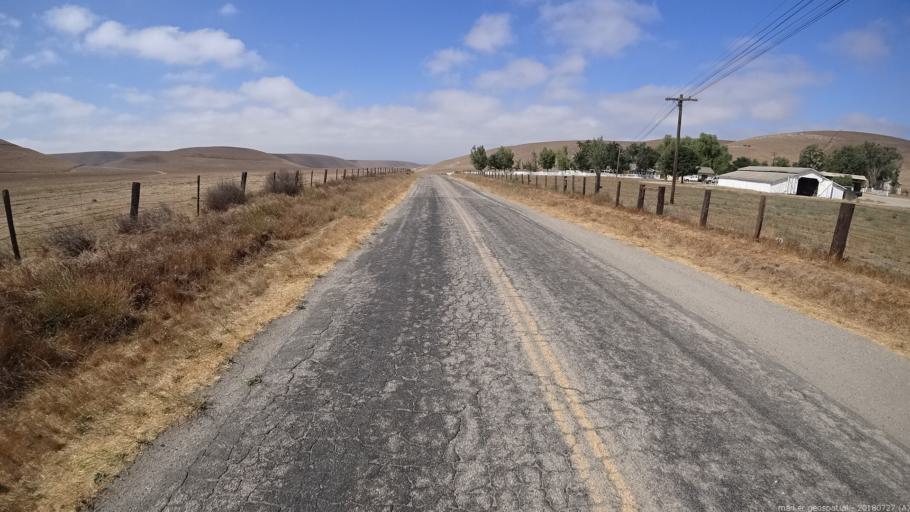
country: US
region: California
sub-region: Monterey County
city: King City
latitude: 36.2448
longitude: -121.0365
